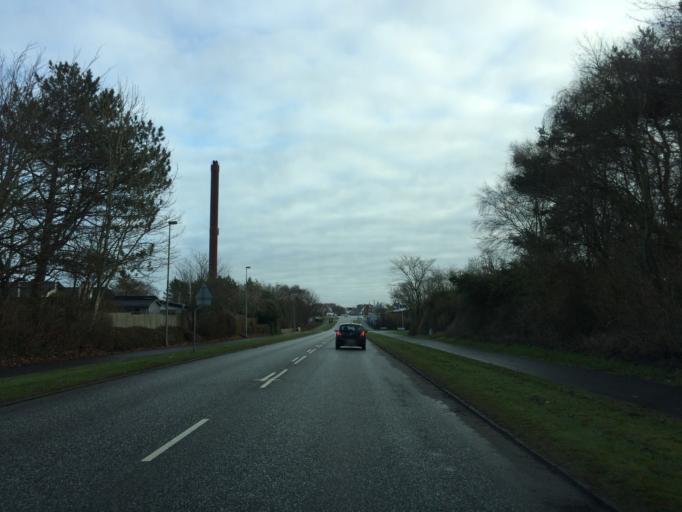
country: DK
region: Central Jutland
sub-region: Struer Kommune
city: Struer
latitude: 56.4888
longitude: 8.5775
